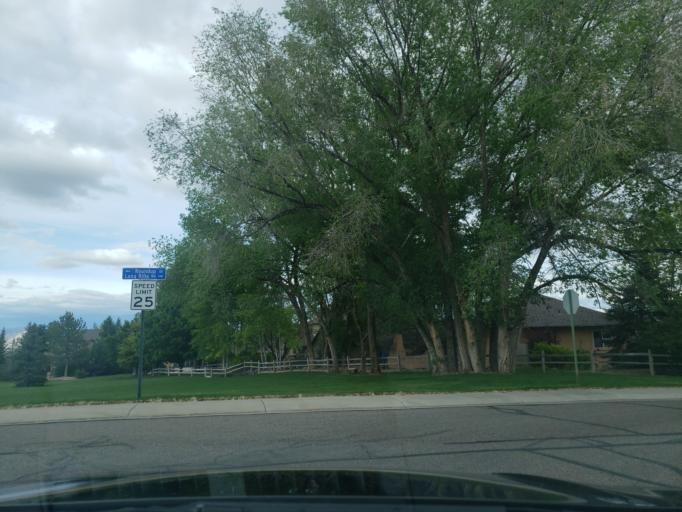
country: US
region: Colorado
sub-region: Mesa County
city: Redlands
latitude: 39.1033
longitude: -108.6680
